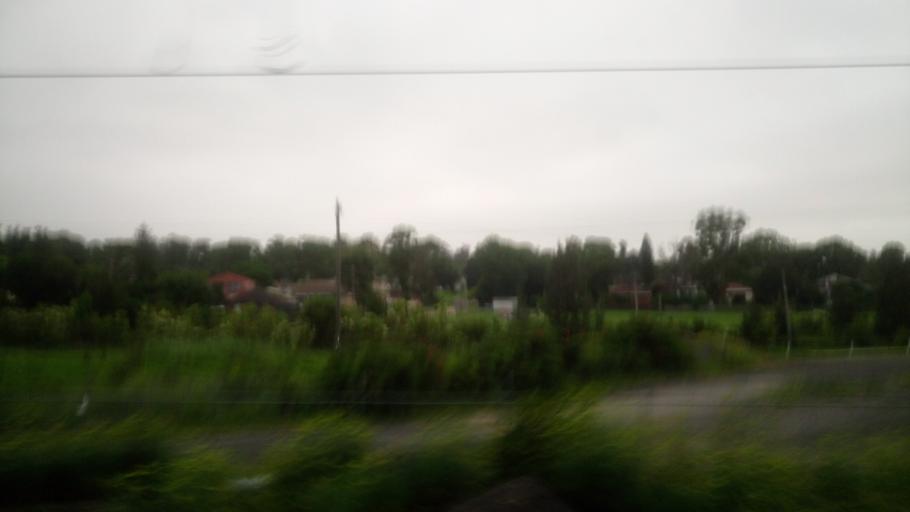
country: AU
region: New South Wales
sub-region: Blacktown
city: Blacktown
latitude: -33.7740
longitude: 150.9320
